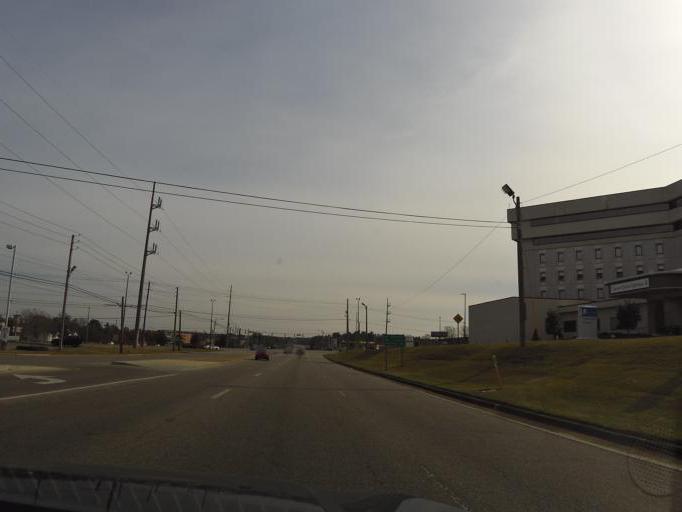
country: US
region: Alabama
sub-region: Houston County
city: Dothan
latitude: 31.2171
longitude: -85.3626
